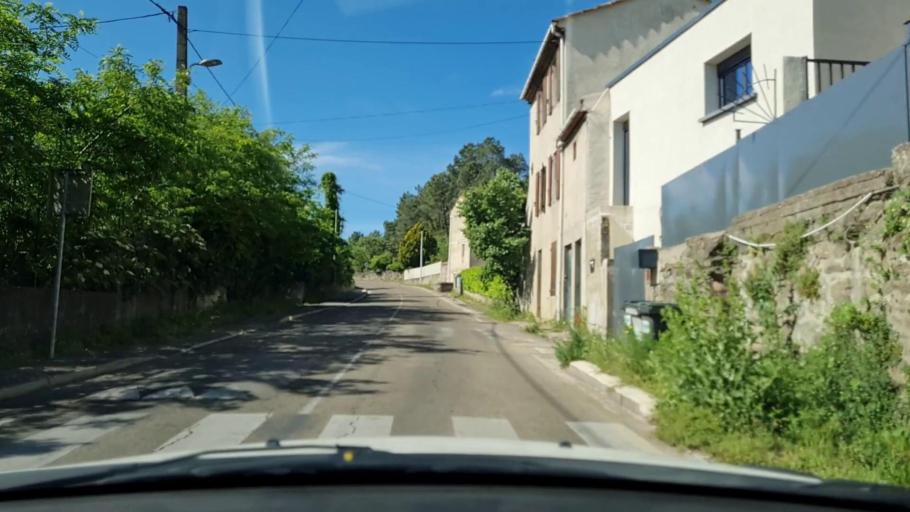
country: FR
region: Languedoc-Roussillon
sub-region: Departement du Gard
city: Cendras
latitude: 44.1422
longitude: 4.0748
